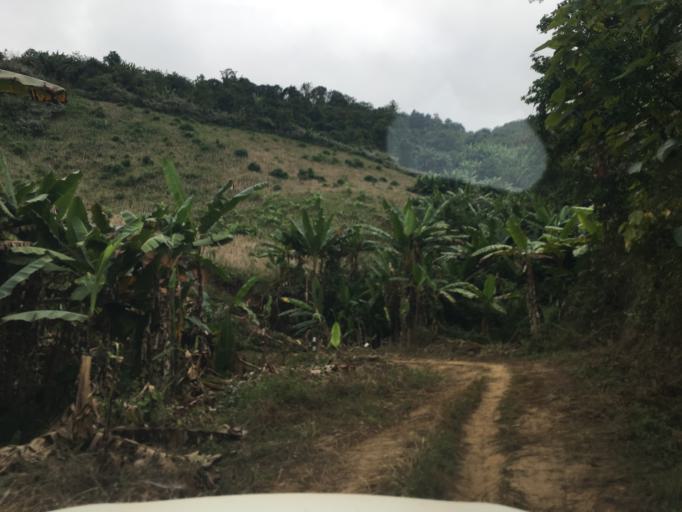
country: LA
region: Houaphan
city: Viengthong
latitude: 19.9351
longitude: 103.2965
